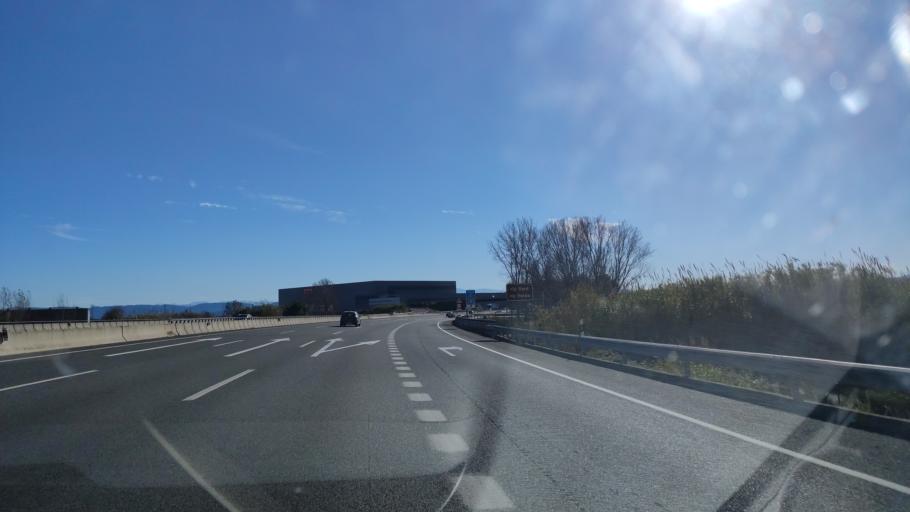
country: ES
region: Valencia
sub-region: Provincia de Valencia
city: Masalaves
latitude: 39.1366
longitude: -0.5246
